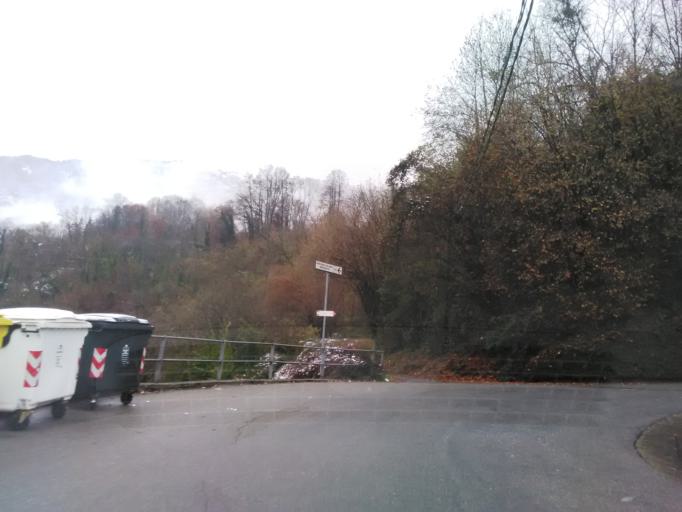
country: IT
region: Piedmont
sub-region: Provincia di Vercelli
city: Quarona
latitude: 45.7829
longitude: 8.2548
